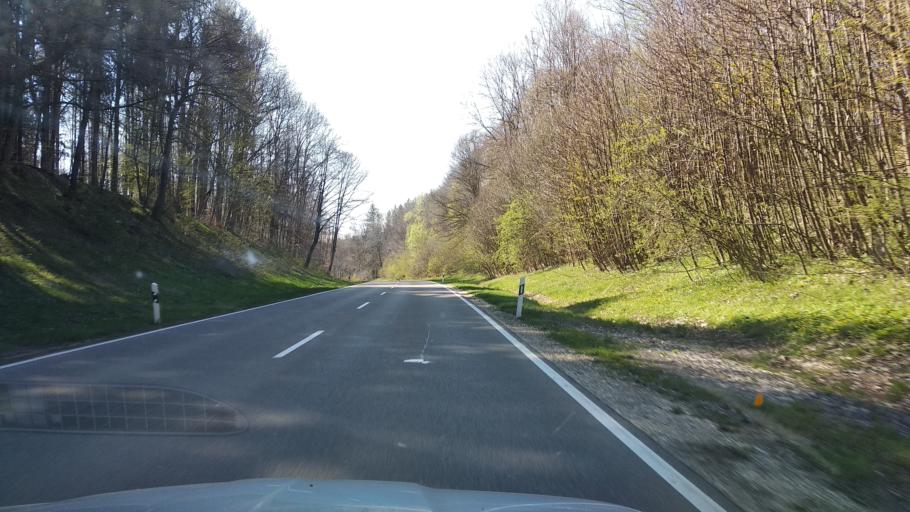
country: DE
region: Bavaria
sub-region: Swabia
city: Erkheim
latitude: 48.0466
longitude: 10.3845
